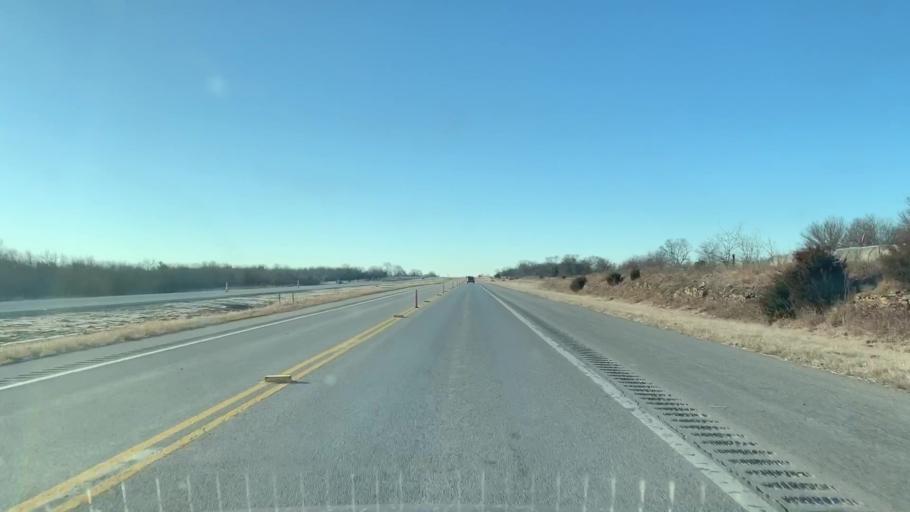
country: US
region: Kansas
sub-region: Bourbon County
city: Fort Scott
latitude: 37.7603
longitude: -94.7050
